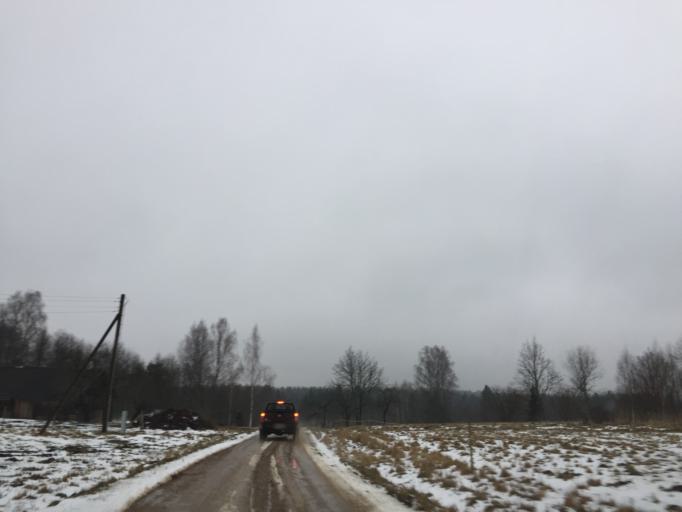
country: LV
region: Seja
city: Loja
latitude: 57.1324
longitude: 24.5990
